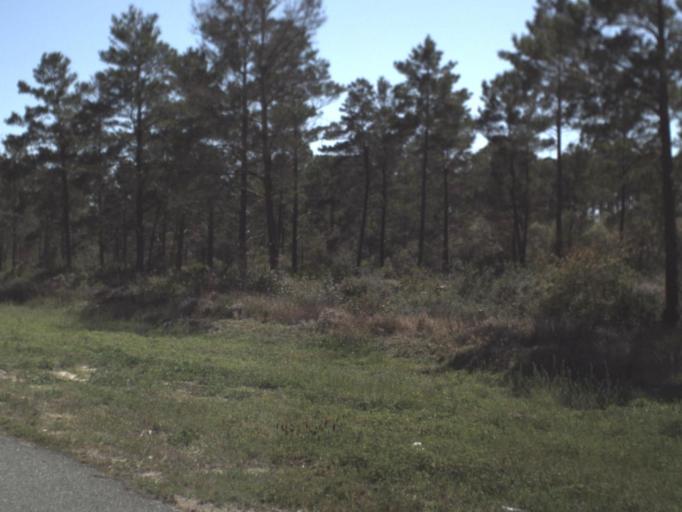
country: US
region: Florida
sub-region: Gulf County
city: Port Saint Joe
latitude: 29.8791
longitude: -85.3411
